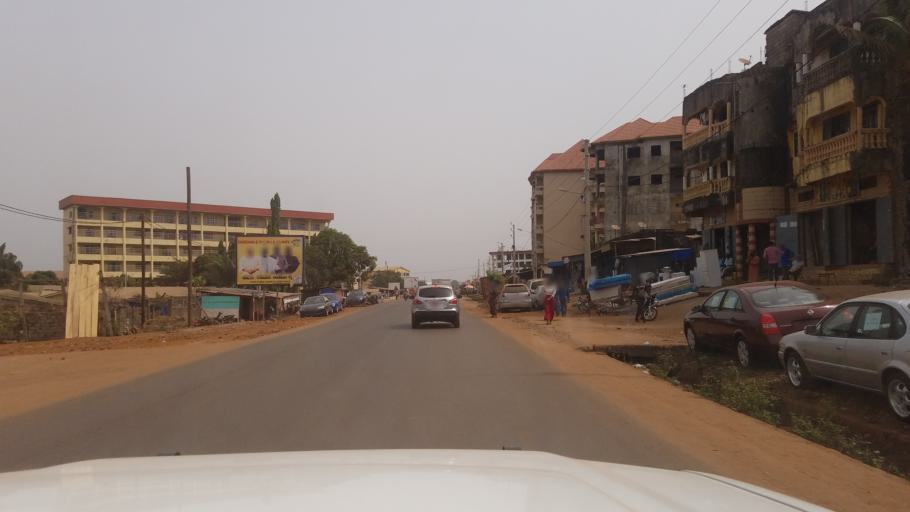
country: GN
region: Conakry
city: Conakry
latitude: 9.6586
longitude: -13.5989
